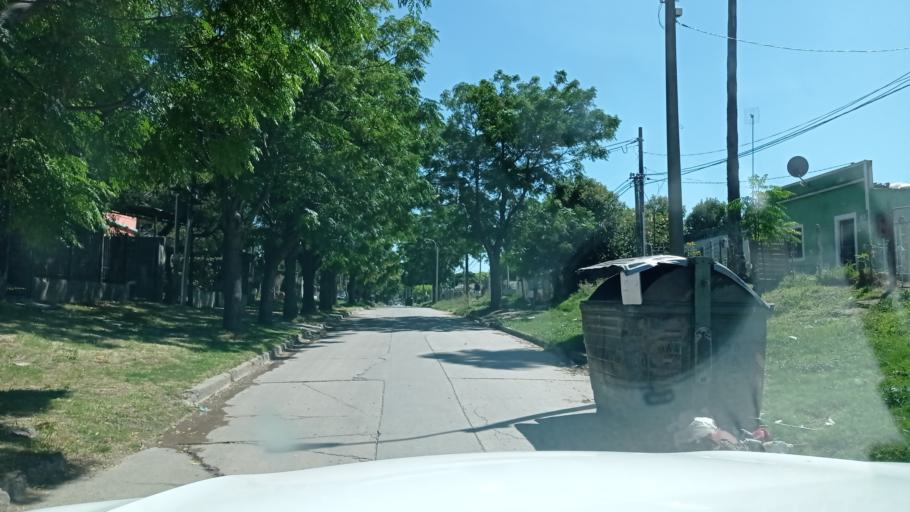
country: UY
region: Montevideo
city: Montevideo
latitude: -34.8659
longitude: -56.2634
